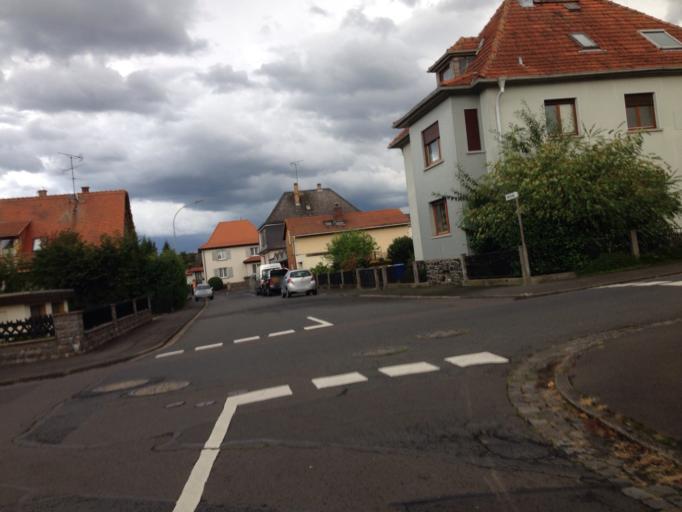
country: DE
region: Hesse
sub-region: Regierungsbezirk Giessen
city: Hungen
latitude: 50.4754
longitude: 8.8906
